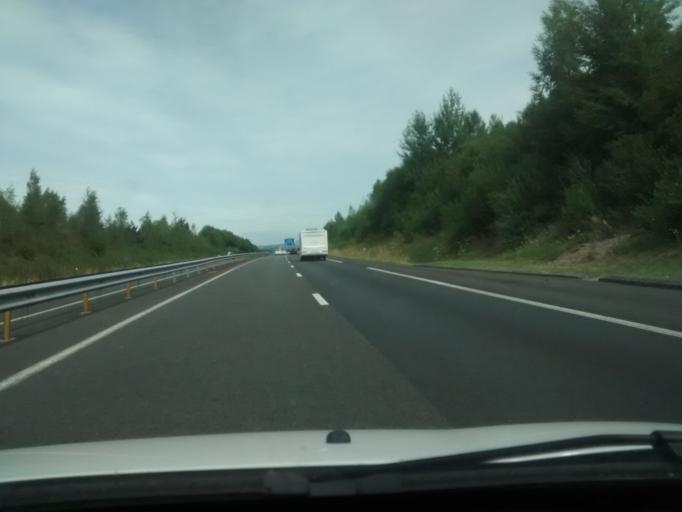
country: FR
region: Lower Normandy
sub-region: Departement de la Manche
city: Saint-James
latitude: 48.5236
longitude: -1.3468
